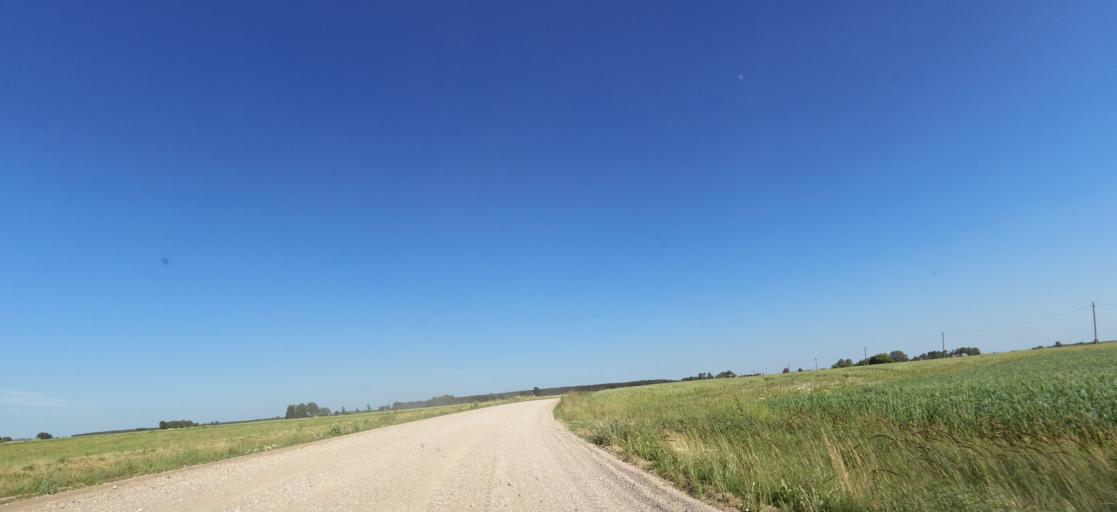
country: LT
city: Vabalninkas
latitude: 56.0263
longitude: 24.6820
